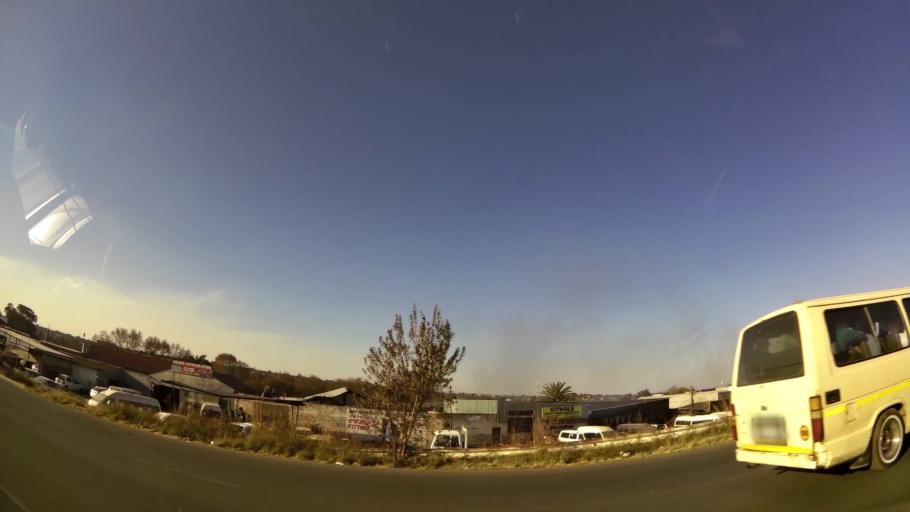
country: ZA
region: Gauteng
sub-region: City of Johannesburg Metropolitan Municipality
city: Roodepoort
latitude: -26.1659
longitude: 27.8708
